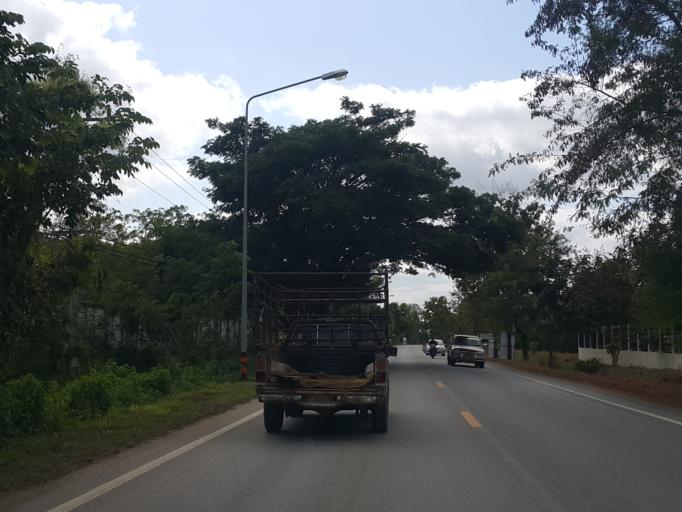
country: TH
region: Lamphun
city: Ban Thi
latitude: 18.6092
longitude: 99.0898
